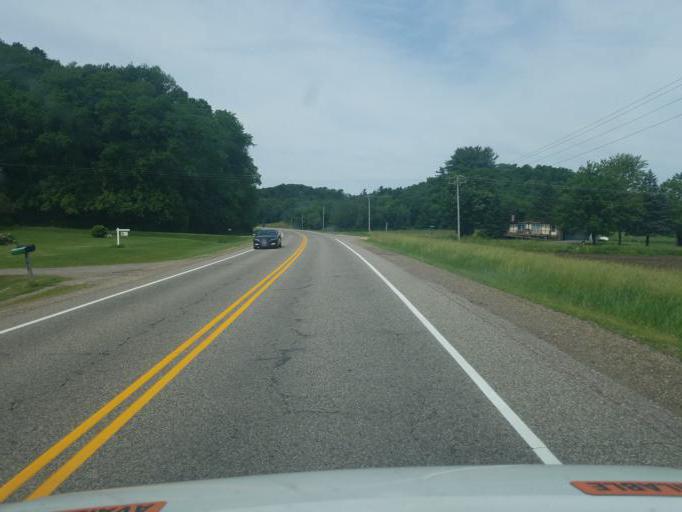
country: US
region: Wisconsin
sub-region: Juneau County
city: New Lisbon
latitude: 43.7903
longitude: -90.1758
